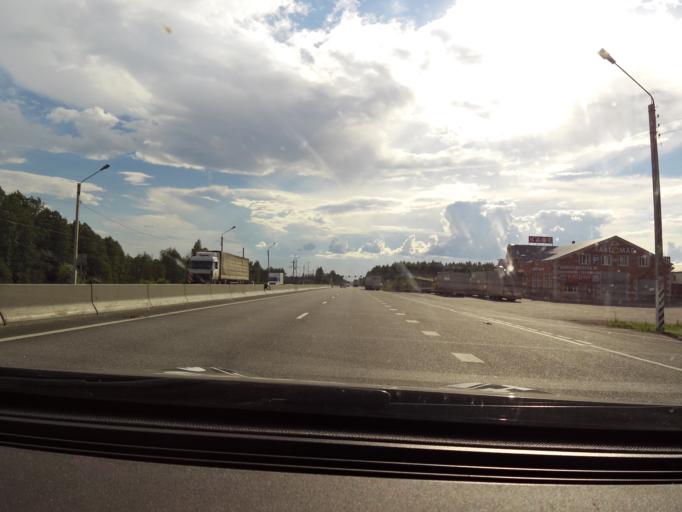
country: RU
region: Vladimir
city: Galitsy
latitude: 56.2438
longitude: 42.8526
